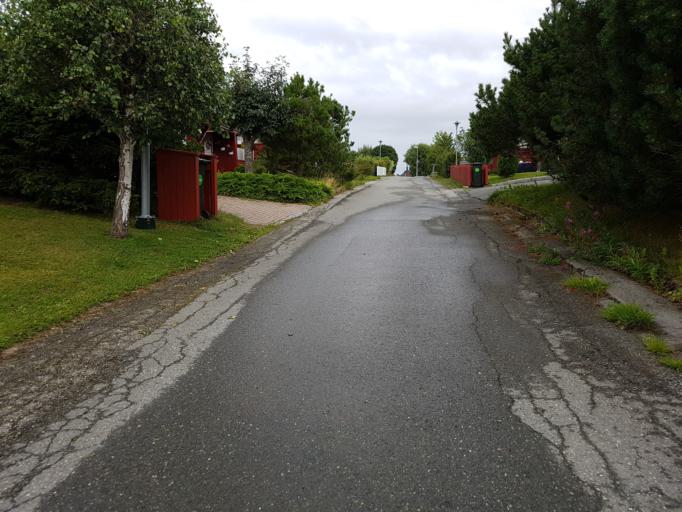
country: NO
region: Sor-Trondelag
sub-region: Trondheim
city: Trondheim
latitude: 63.3916
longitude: 10.3609
